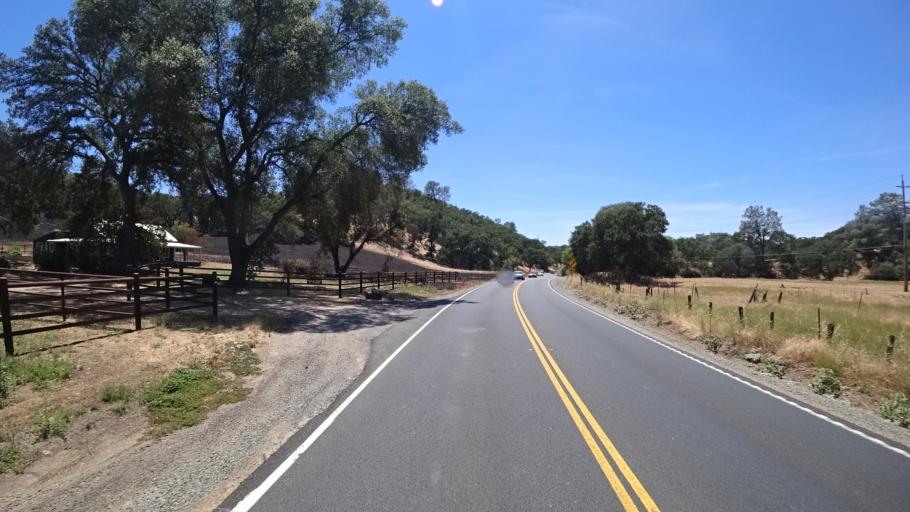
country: US
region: California
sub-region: Calaveras County
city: Rancho Calaveras
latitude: 38.1337
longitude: -120.8694
